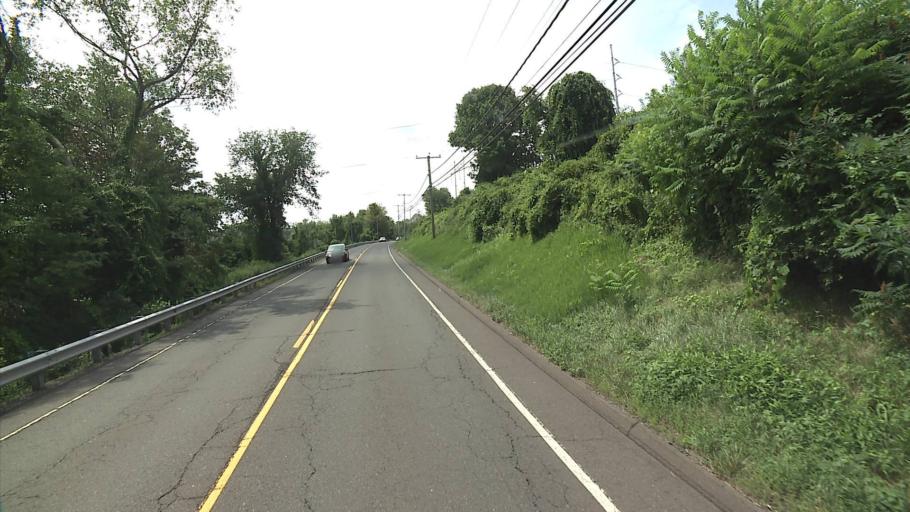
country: US
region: Connecticut
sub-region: Middlesex County
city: Durham
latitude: 41.5117
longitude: -72.6697
